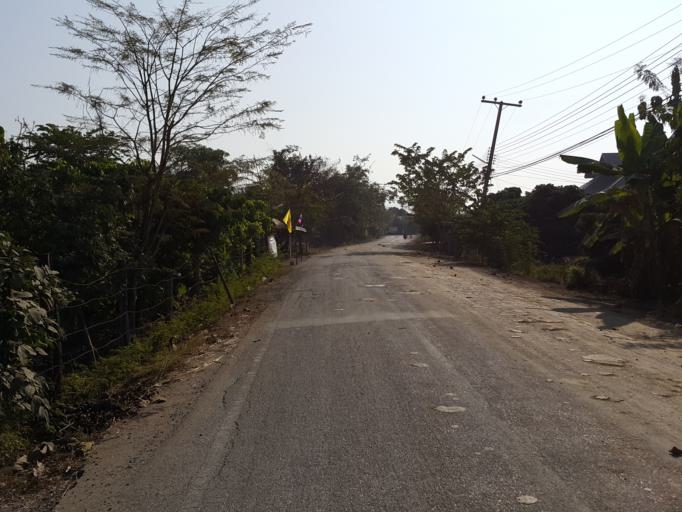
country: TH
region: Chiang Mai
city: San Kamphaeng
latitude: 18.6969
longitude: 99.1107
